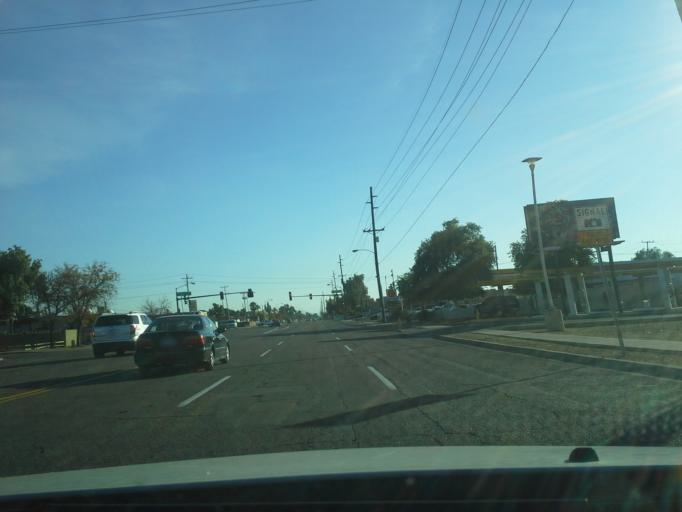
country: US
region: Arizona
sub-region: Maricopa County
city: Glendale
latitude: 33.5977
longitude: -112.1340
